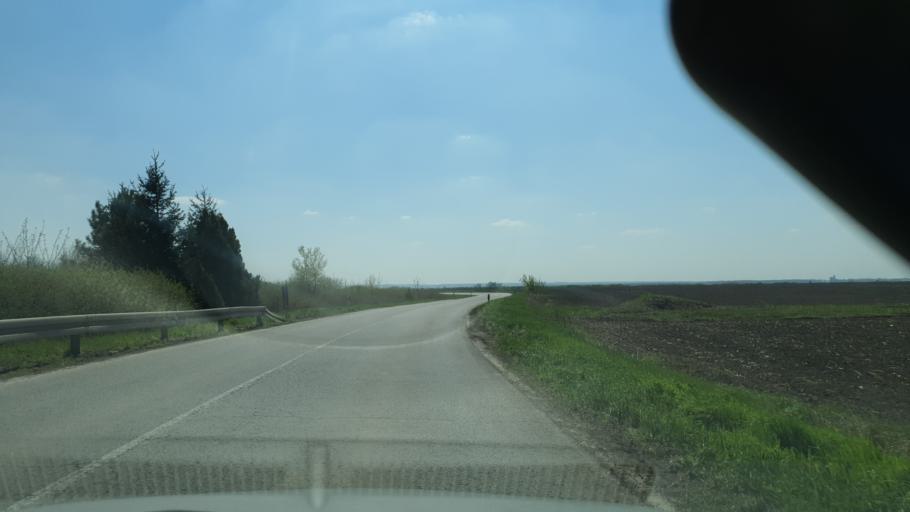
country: RS
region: Autonomna Pokrajina Vojvodina
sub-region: Juznobacki Okrug
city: Backa Palanka
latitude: 45.3176
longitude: 19.4427
